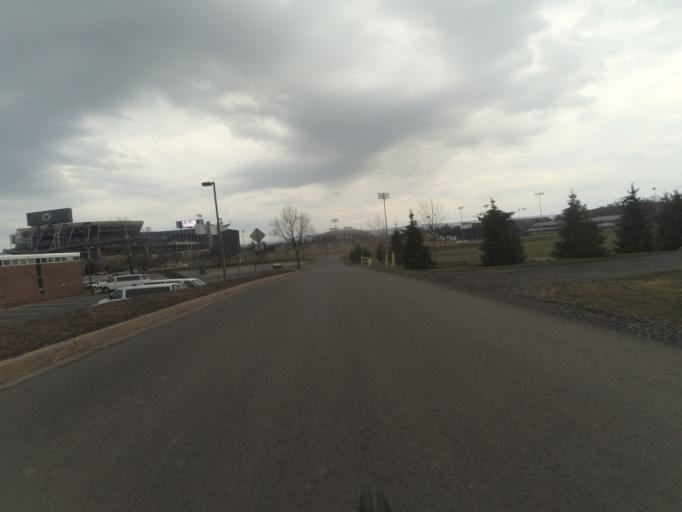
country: US
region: Pennsylvania
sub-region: Centre County
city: State College
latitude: 40.8127
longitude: -77.8614
